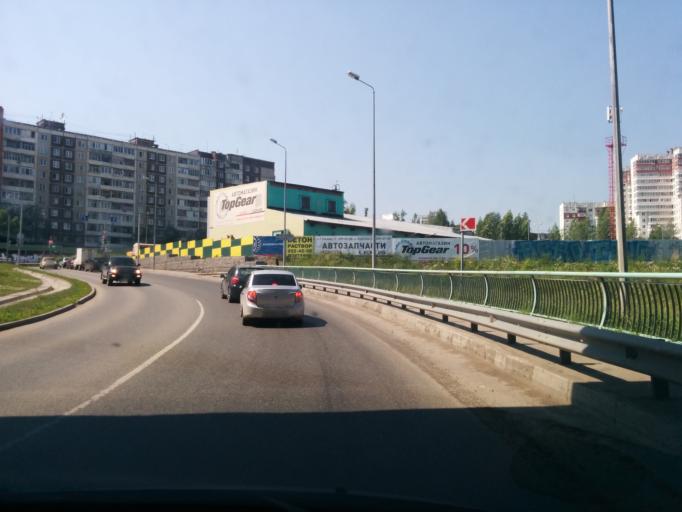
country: RU
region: Perm
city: Perm
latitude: 58.0021
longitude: 56.3161
